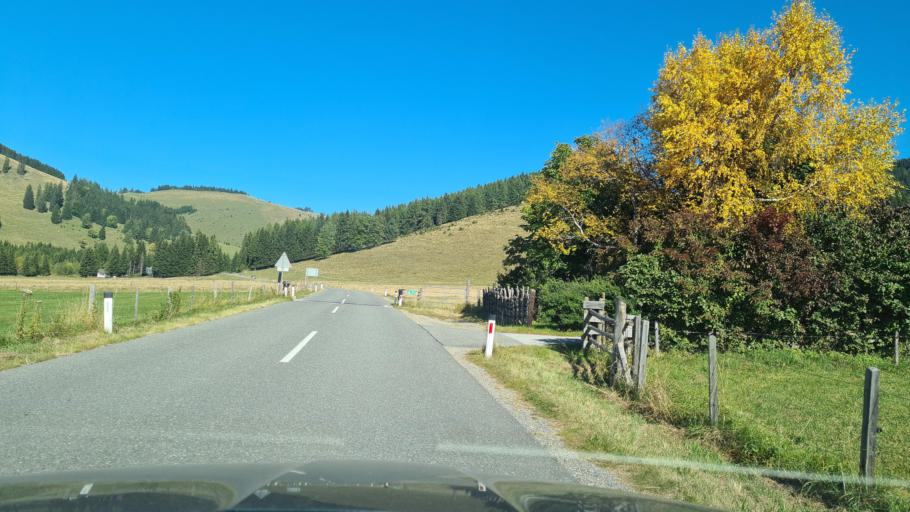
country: AT
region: Styria
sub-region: Politischer Bezirk Weiz
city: Passail
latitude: 47.3432
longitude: 15.4789
